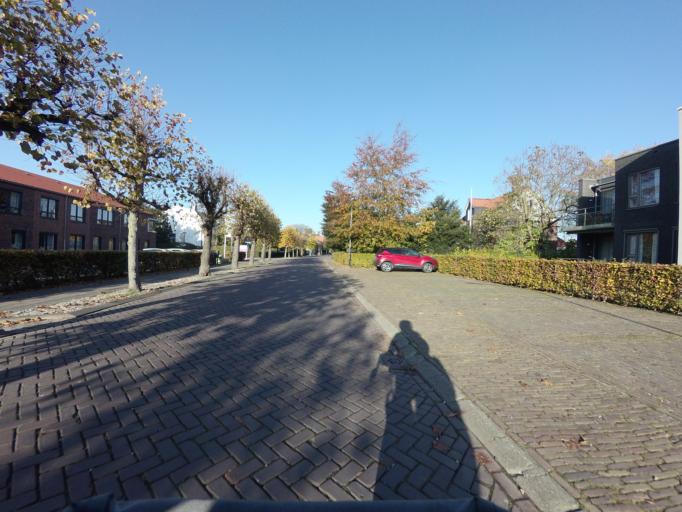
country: NL
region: North Brabant
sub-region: Gemeente Woudrichem
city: Woudrichem
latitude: 51.7840
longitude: 5.0543
